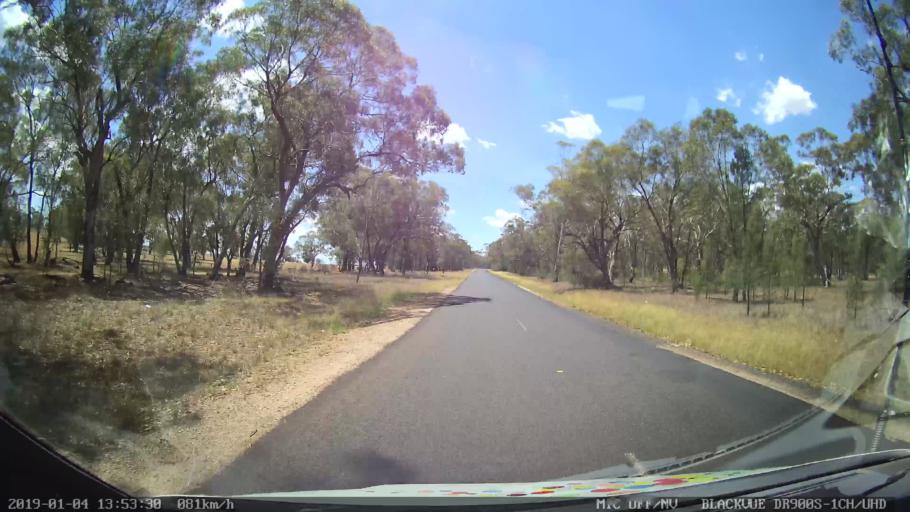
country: AU
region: New South Wales
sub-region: Dubbo Municipality
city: Dubbo
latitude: -32.3826
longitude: 148.5749
